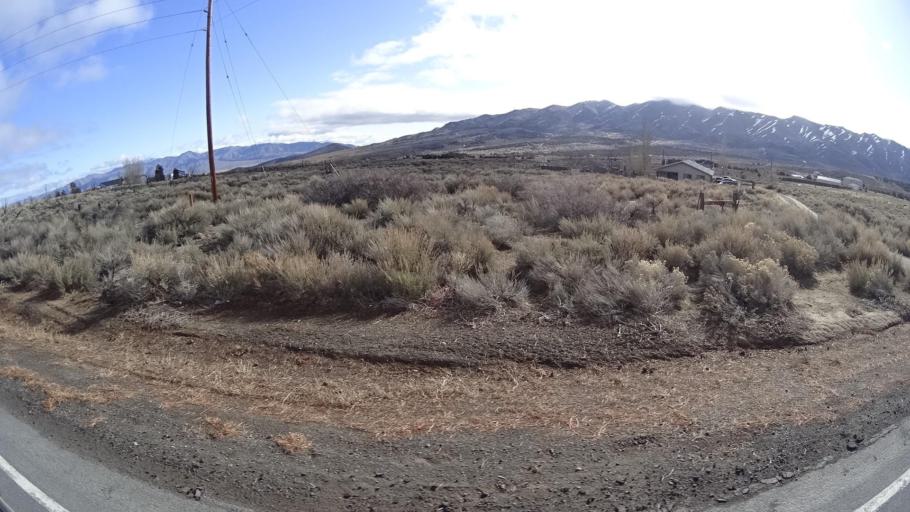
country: US
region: Nevada
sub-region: Washoe County
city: Cold Springs
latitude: 39.7876
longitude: -119.8991
